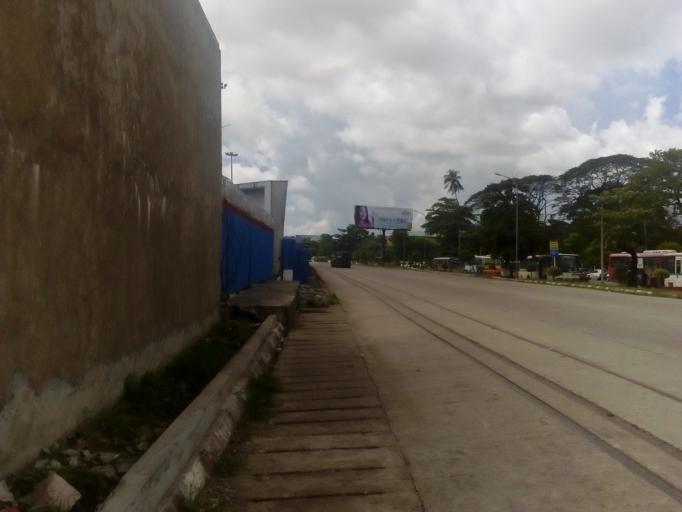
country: MM
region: Yangon
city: Yangon
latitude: 16.7778
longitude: 96.1357
